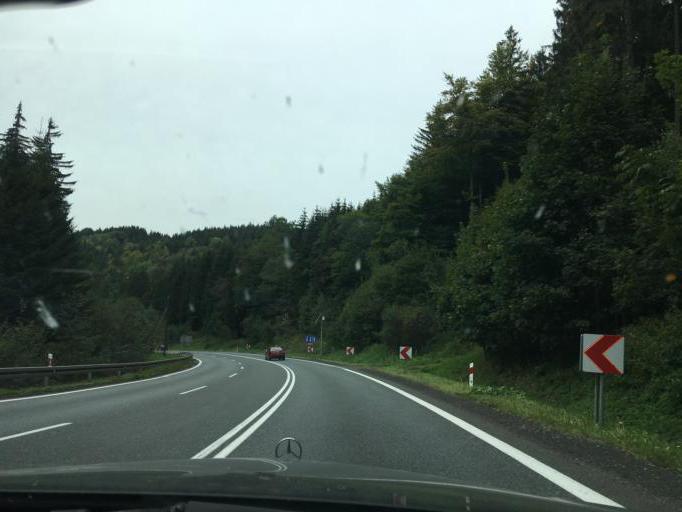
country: PL
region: Lower Silesian Voivodeship
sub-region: Powiat klodzki
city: Lewin Klodzki
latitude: 50.4111
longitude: 16.3224
